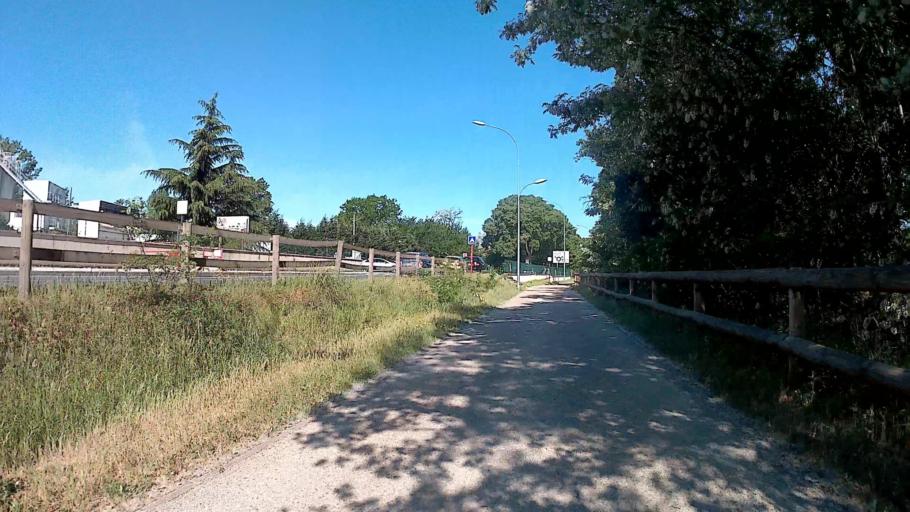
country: FR
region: Aquitaine
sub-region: Departement de la Gironde
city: Villenave-d'Ornon
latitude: 44.7804
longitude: -0.5349
